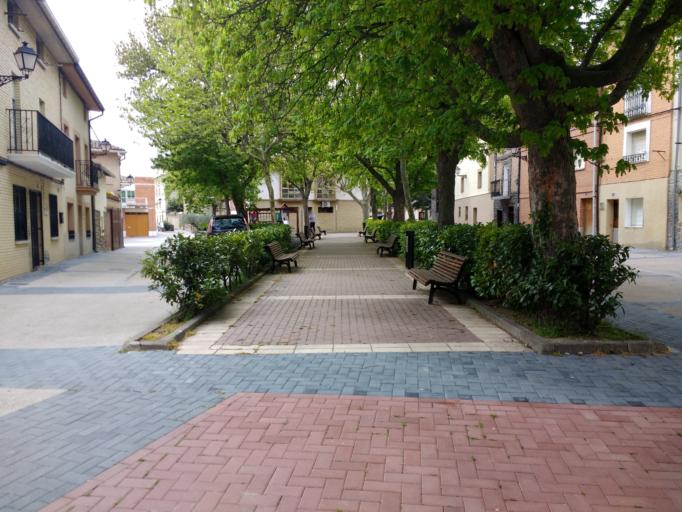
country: ES
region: La Rioja
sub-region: Provincia de La Rioja
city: Leiva
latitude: 42.5035
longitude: -3.0467
